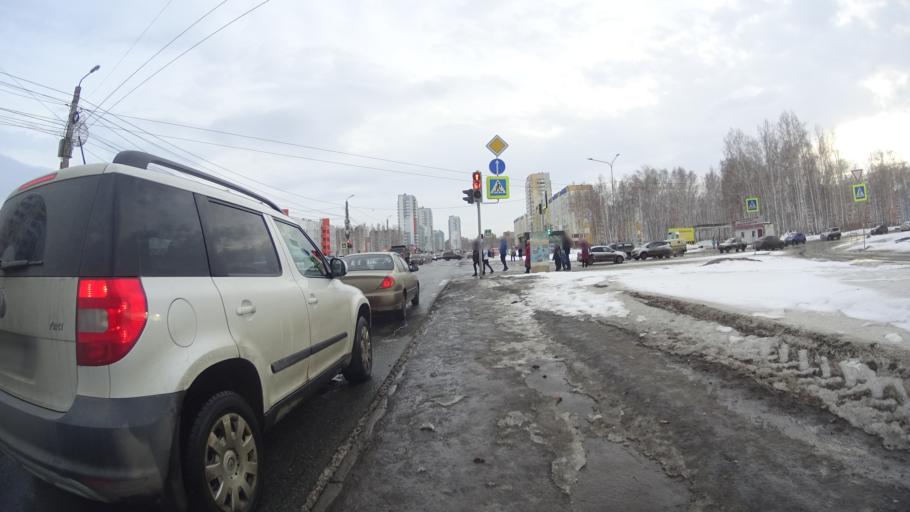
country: RU
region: Chelyabinsk
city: Roshchino
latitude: 55.2077
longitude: 61.2842
